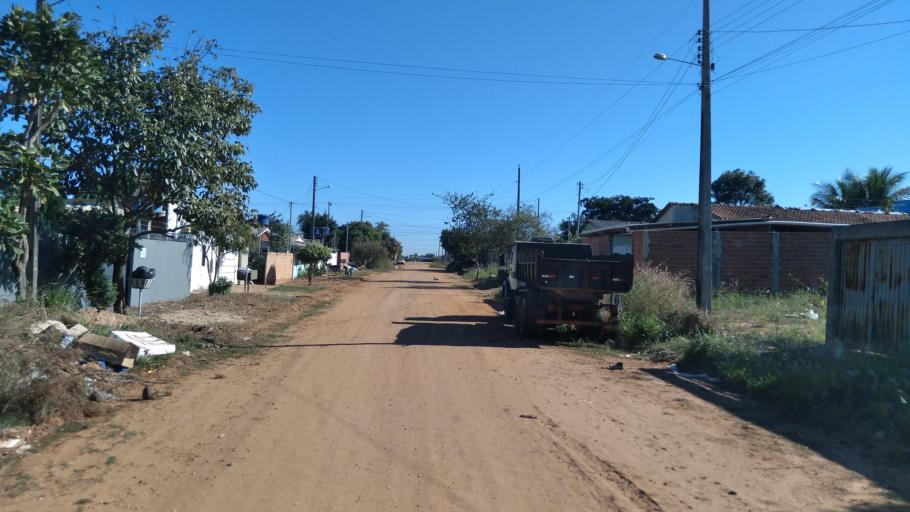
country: BR
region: Goias
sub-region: Mineiros
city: Mineiros
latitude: -17.5909
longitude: -52.5568
